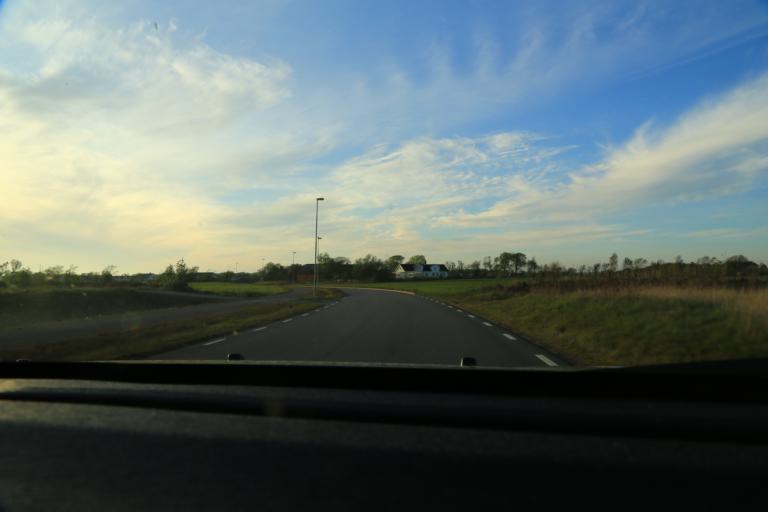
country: SE
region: Halland
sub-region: Varbergs Kommun
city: Traslovslage
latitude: 57.0581
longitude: 12.2942
